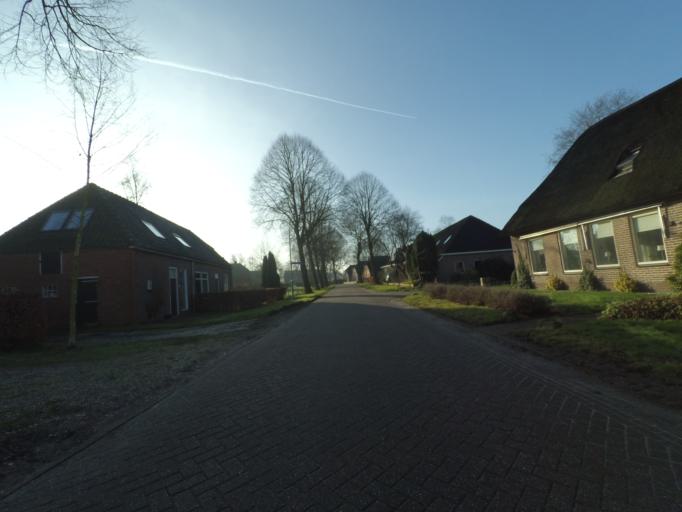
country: NL
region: Drenthe
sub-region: Gemeente Assen
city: Assen
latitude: 52.8832
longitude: 6.6443
